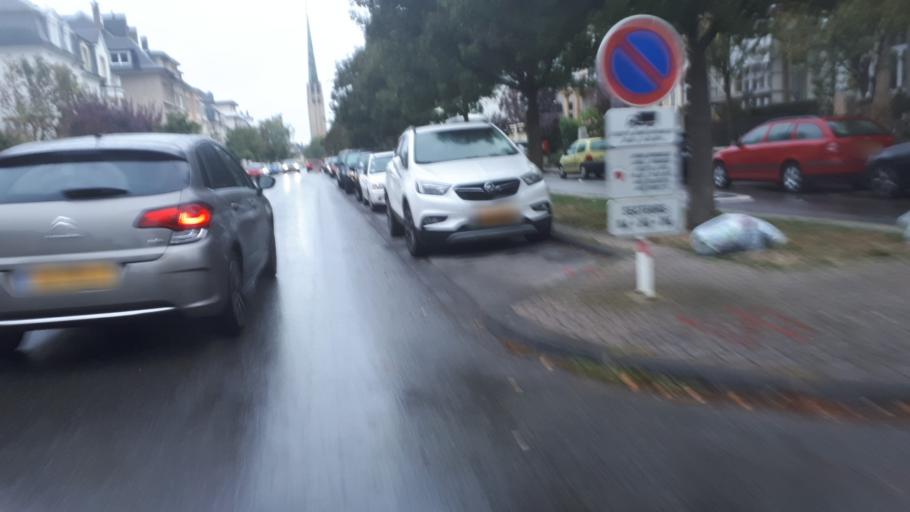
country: LU
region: Luxembourg
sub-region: Canton de Luxembourg
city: Luxembourg
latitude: 49.6103
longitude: 6.1120
